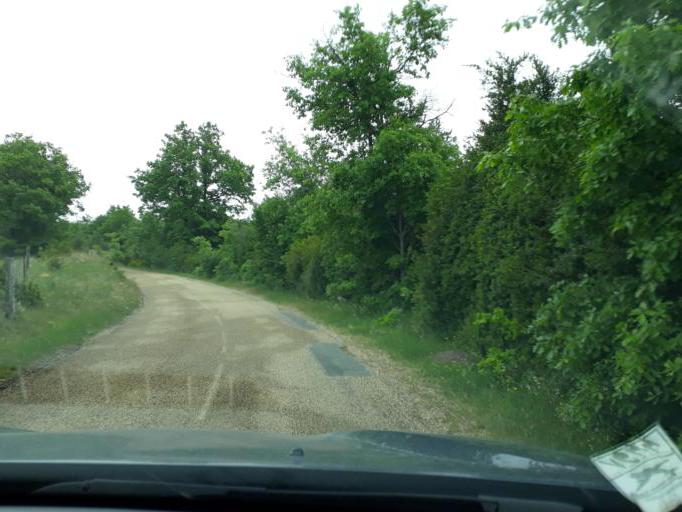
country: FR
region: Languedoc-Roussillon
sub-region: Departement de l'Herault
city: Lodeve
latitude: 43.8480
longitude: 3.2675
